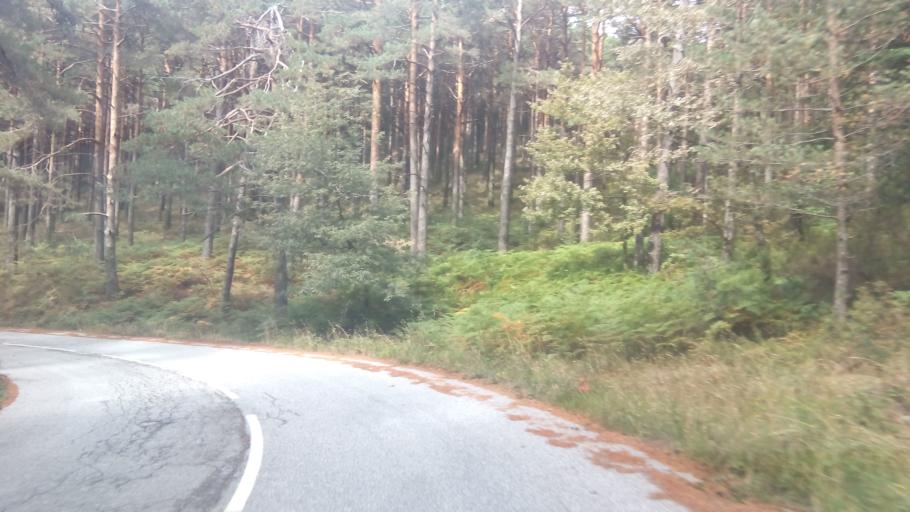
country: PT
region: Vila Real
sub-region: Mesao Frio
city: Mesao Frio
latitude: 41.2796
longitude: -7.9178
